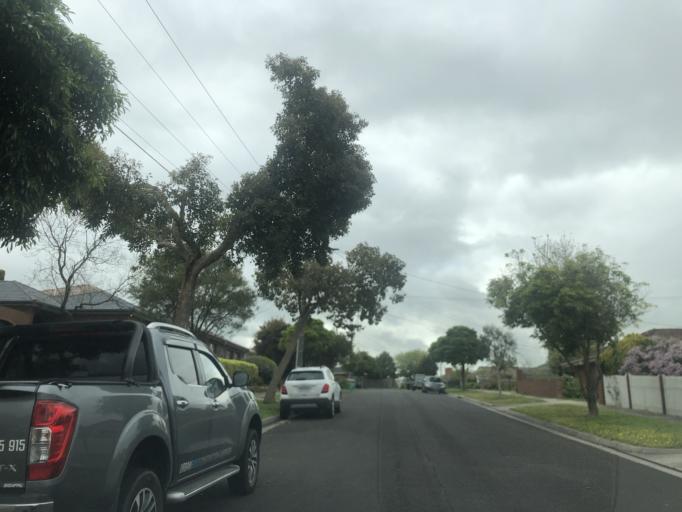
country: AU
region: Victoria
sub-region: Greater Dandenong
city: Dandenong North
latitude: -37.9637
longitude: 145.2188
